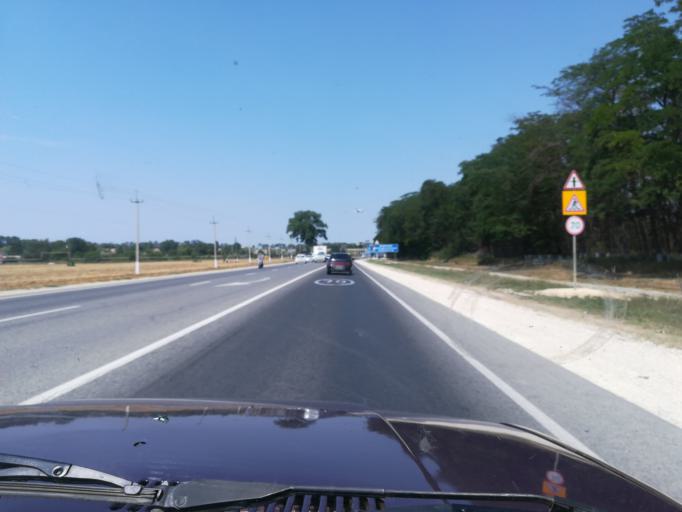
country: RU
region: Krasnodarskiy
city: Tsibanobalka
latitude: 44.9748
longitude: 37.3207
